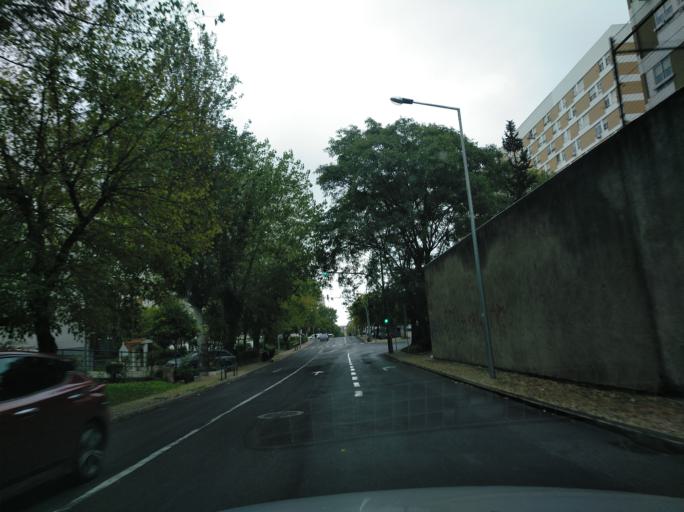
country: PT
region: Lisbon
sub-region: Loures
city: Sacavem
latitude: 38.7837
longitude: -9.1147
